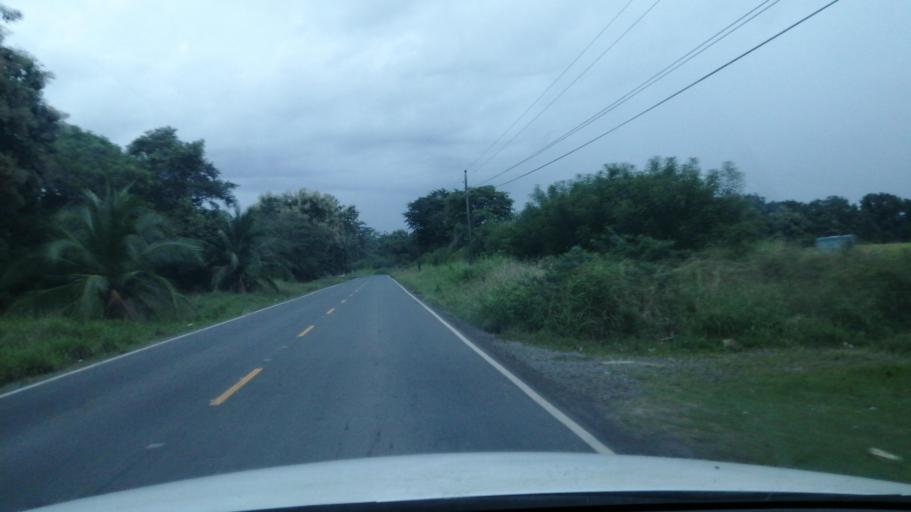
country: PA
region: Chiriqui
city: Alanje
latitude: 8.3953
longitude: -82.4936
